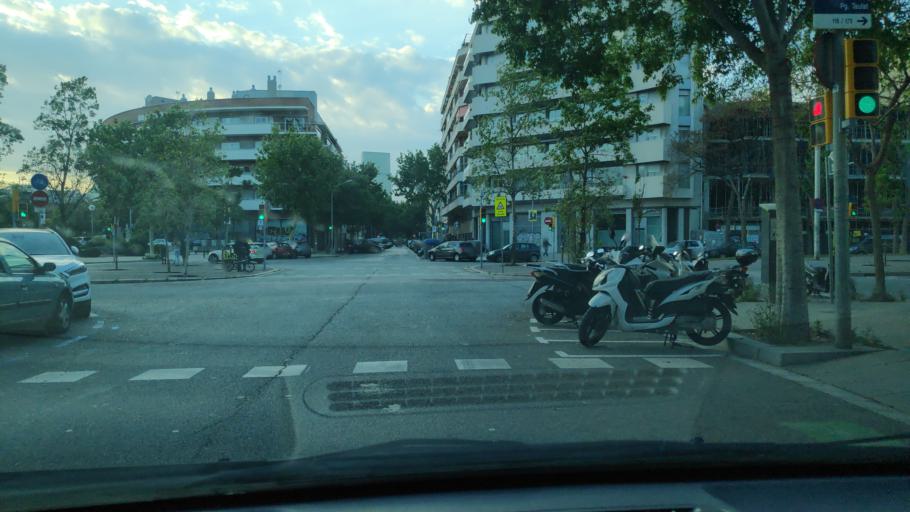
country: ES
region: Catalonia
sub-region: Provincia de Barcelona
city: Sant Marti
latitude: 41.4009
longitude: 2.2083
